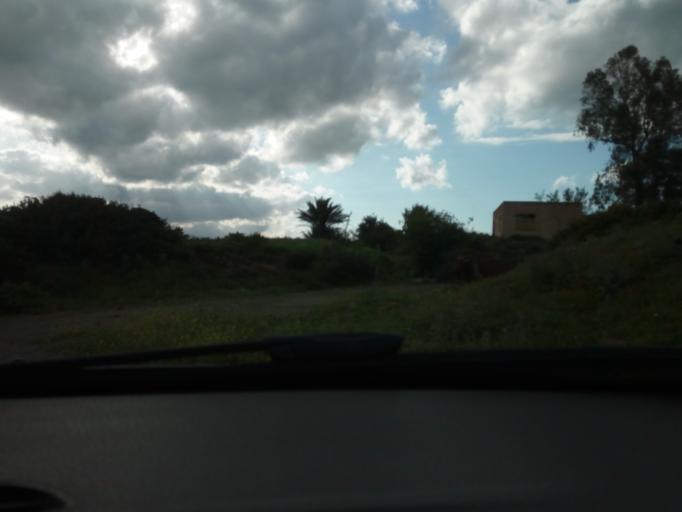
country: DZ
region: Tipaza
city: El Affroun
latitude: 36.3745
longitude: 2.5167
